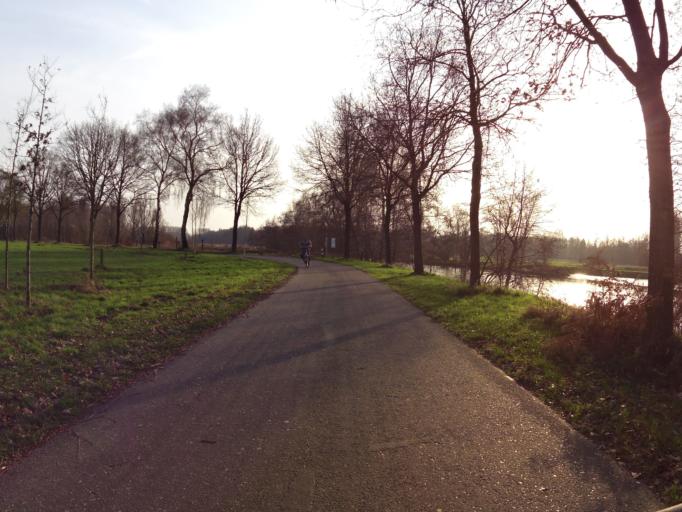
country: NL
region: North Brabant
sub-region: Gemeente Vught
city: Vught
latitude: 51.6634
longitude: 5.3055
